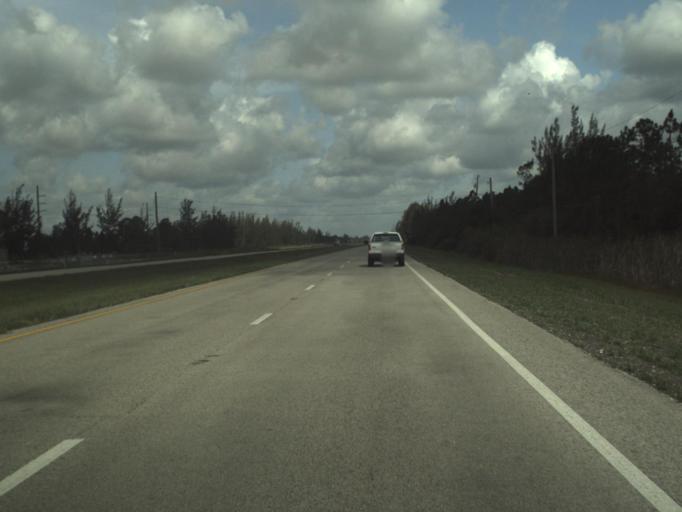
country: US
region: Florida
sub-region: Palm Beach County
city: Limestone Creek
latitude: 26.8822
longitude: -80.2602
